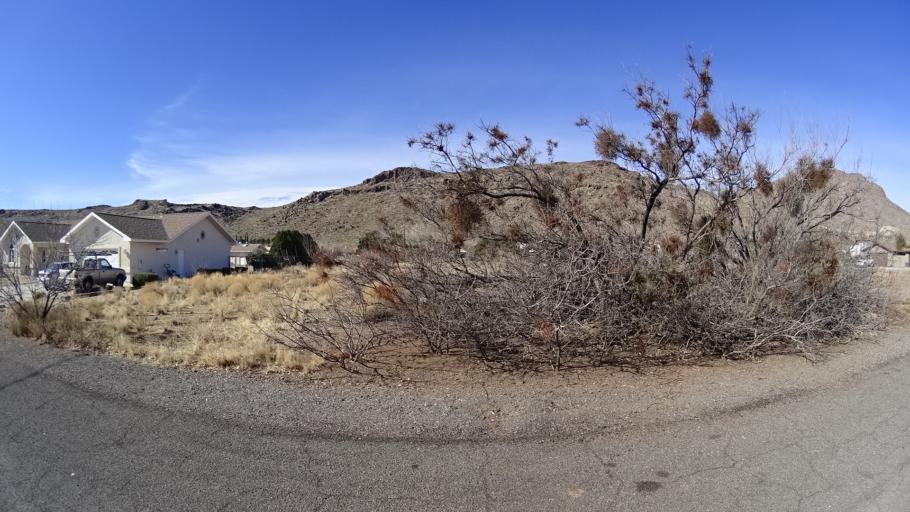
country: US
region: Arizona
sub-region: Mohave County
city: New Kingman-Butler
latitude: 35.2618
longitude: -114.0432
